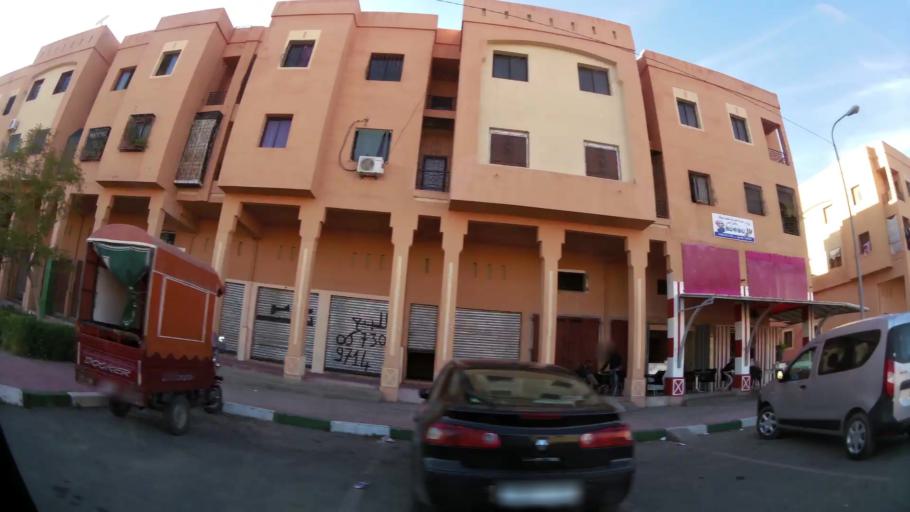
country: MA
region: Marrakech-Tensift-Al Haouz
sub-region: Marrakech
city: Marrakesh
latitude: 31.7641
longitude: -8.1120
